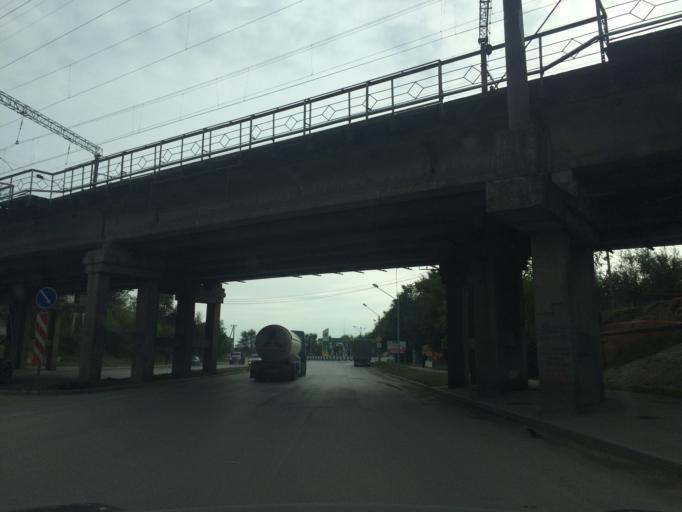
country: RU
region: Rostov
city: Kalinin
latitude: 47.1966
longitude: 39.6136
